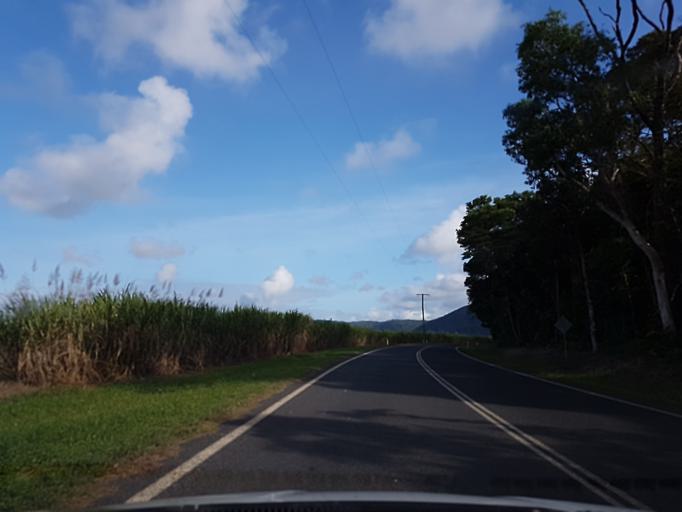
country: AU
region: Queensland
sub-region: Cairns
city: Port Douglas
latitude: -16.2707
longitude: 145.3921
